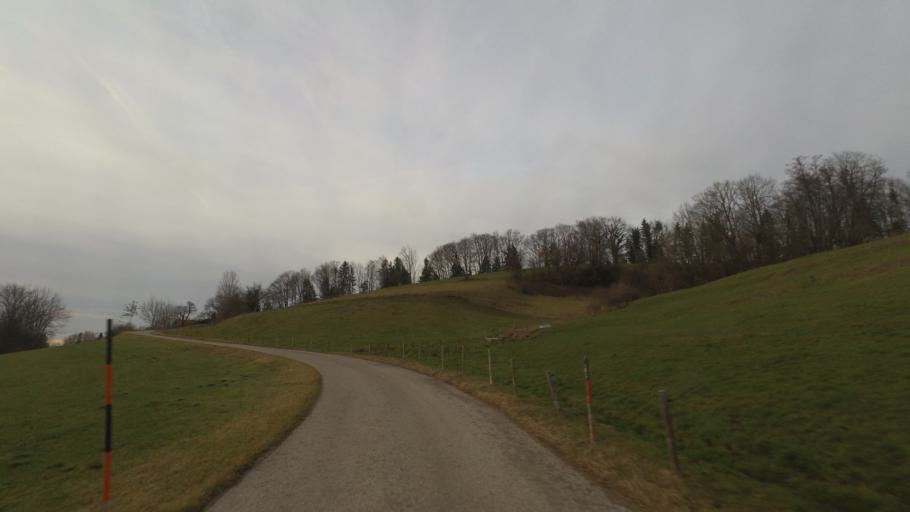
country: DE
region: Bavaria
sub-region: Upper Bavaria
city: Ubersee
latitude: 47.8087
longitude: 12.5079
